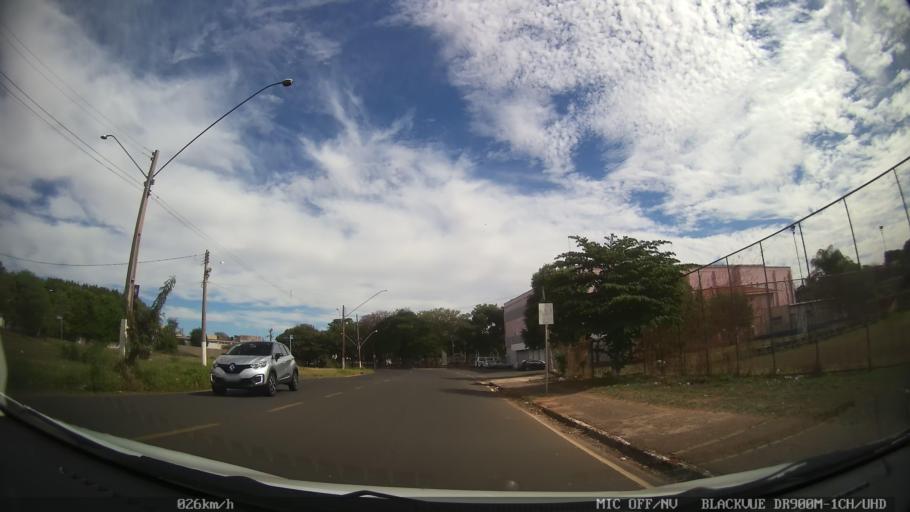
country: BR
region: Sao Paulo
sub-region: Catanduva
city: Catanduva
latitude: -21.1404
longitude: -48.9615
